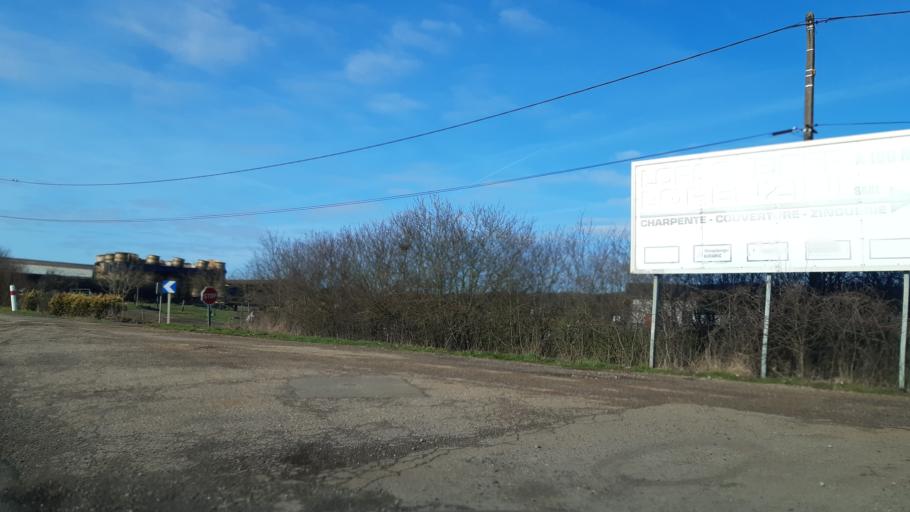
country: FR
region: Lorraine
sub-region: Departement de la Moselle
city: Audun-le-Tiche
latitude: 49.4559
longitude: 5.9558
